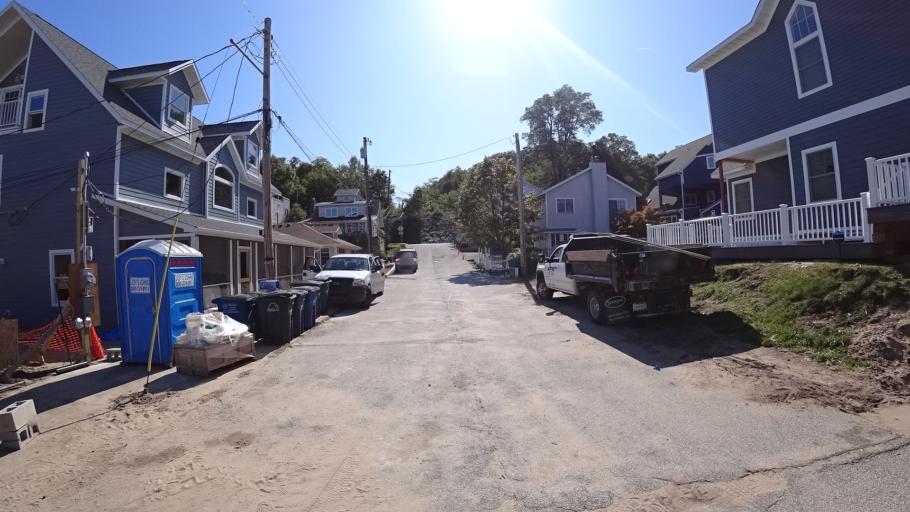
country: US
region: Indiana
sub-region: LaPorte County
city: Michigan City
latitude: 41.7315
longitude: -86.8875
